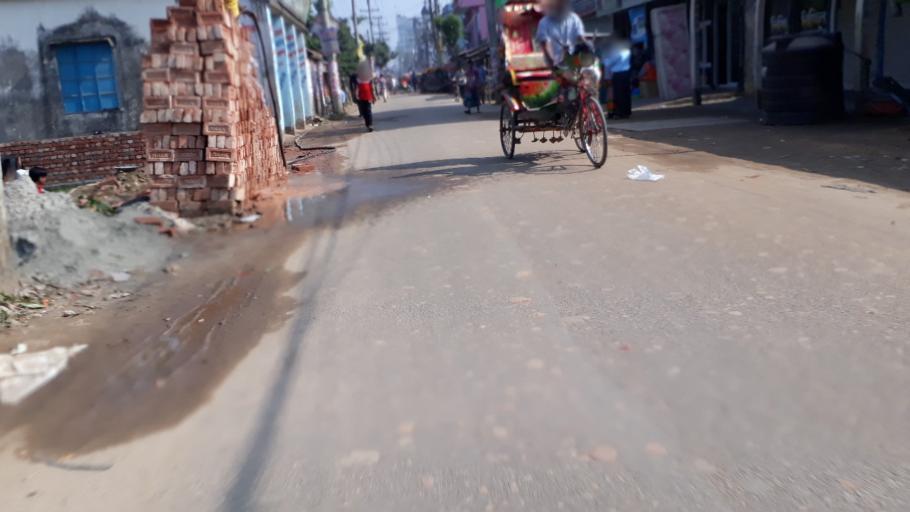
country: BD
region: Dhaka
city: Tungi
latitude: 23.8498
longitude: 90.2812
